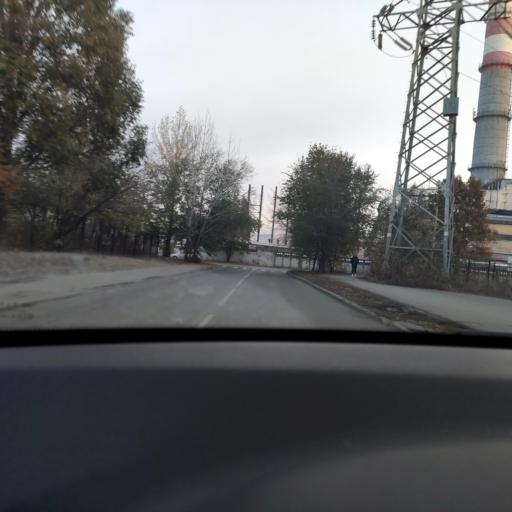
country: RU
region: Samara
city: Samara
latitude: 53.2142
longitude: 50.2025
